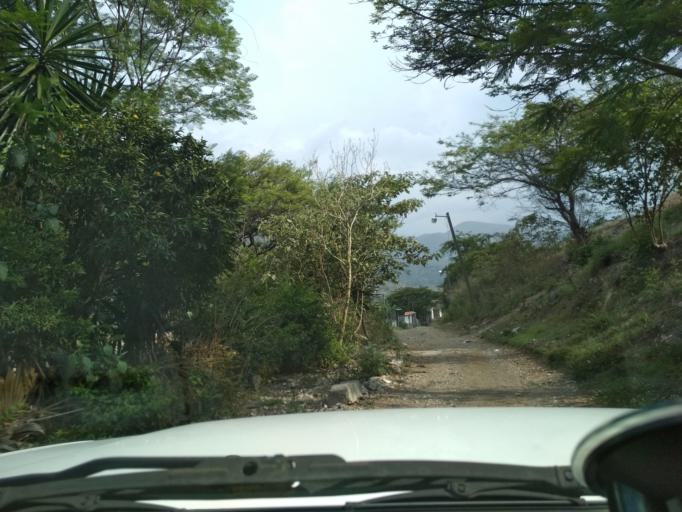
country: MX
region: Veracruz
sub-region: Nogales
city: Agricola Lazaro Cardenas
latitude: 18.7982
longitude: -97.1960
